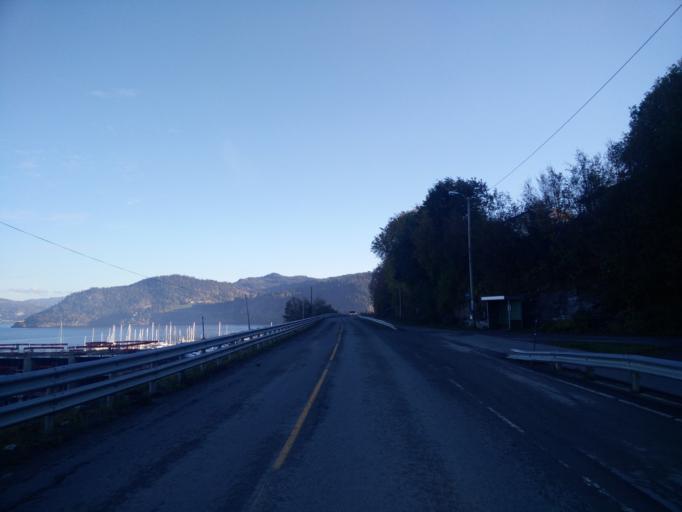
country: NO
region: Sor-Trondelag
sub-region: Skaun
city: Borsa
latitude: 63.3346
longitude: 10.0657
